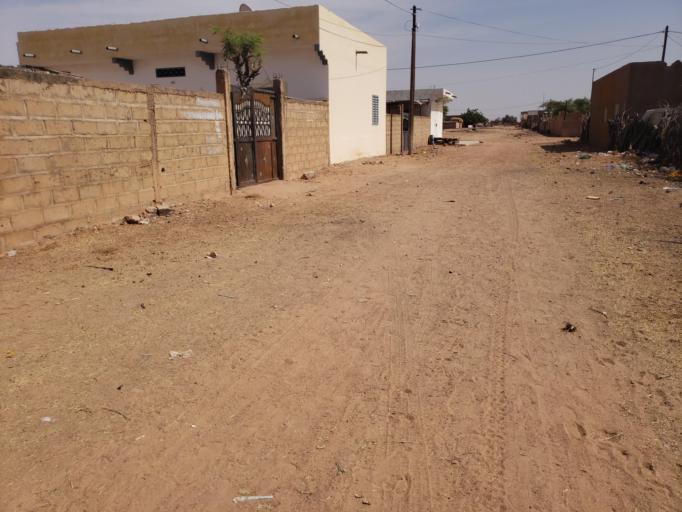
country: SN
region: Matam
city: Ranerou
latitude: 15.3001
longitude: -13.9623
